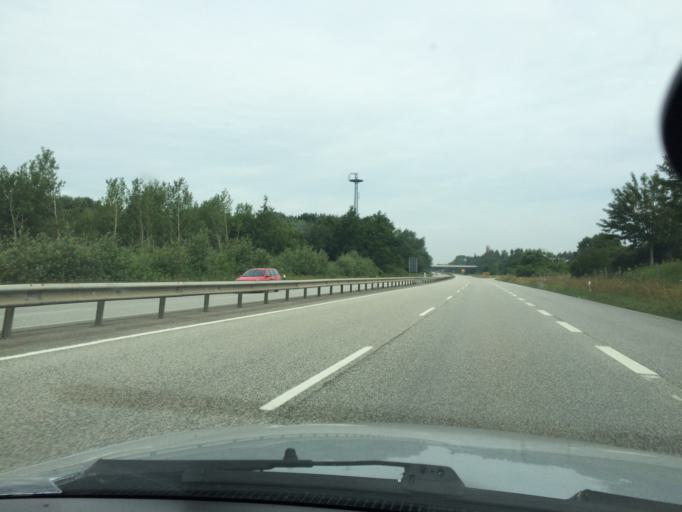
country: DE
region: Schleswig-Holstein
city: Flensburg
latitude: 54.7650
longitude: 9.4261
